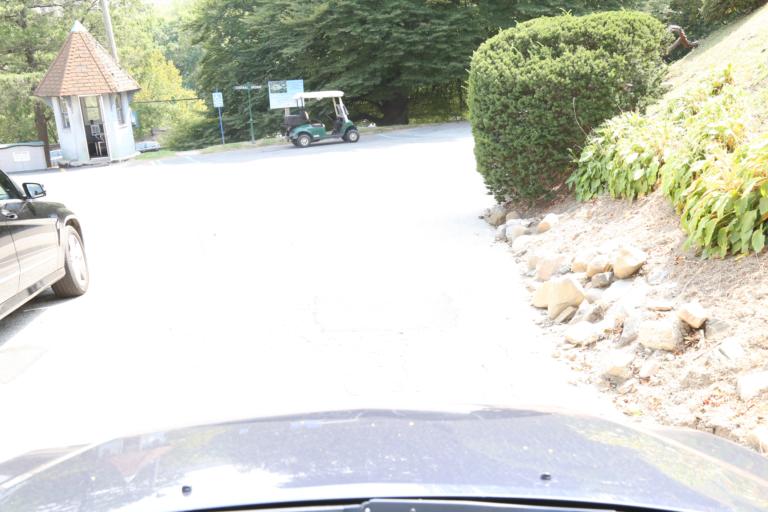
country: US
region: New York
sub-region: Bronx
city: Eastchester
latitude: 40.8949
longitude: -73.8642
